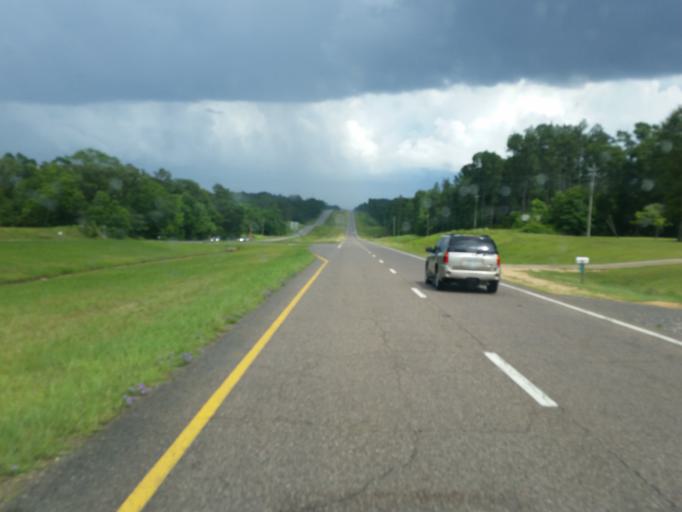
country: US
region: Mississippi
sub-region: George County
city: Lucedale
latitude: 30.9192
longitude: -88.5016
